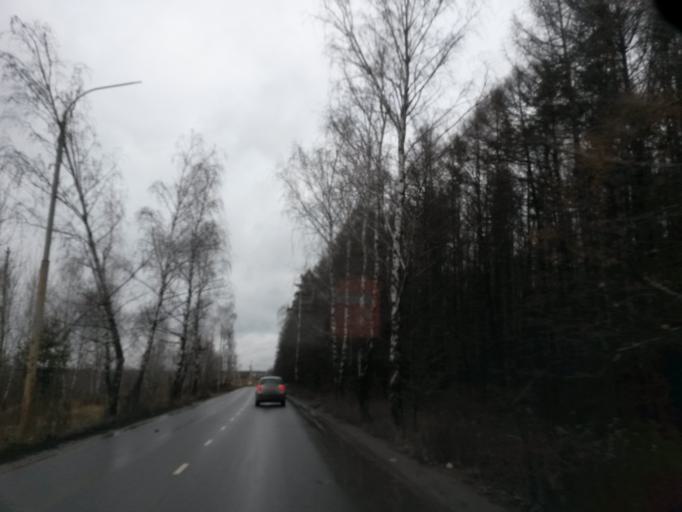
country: RU
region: Moskovskaya
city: Shcherbinka
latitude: 55.5126
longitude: 37.5920
